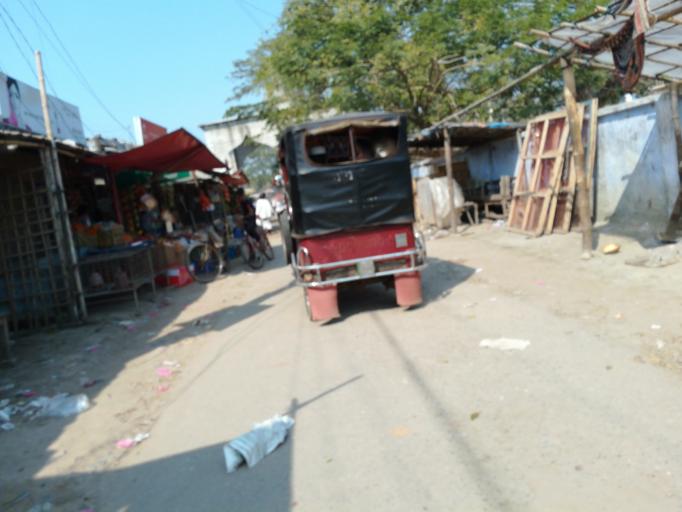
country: BD
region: Khulna
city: Morrelgonj
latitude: 22.6640
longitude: 89.7586
